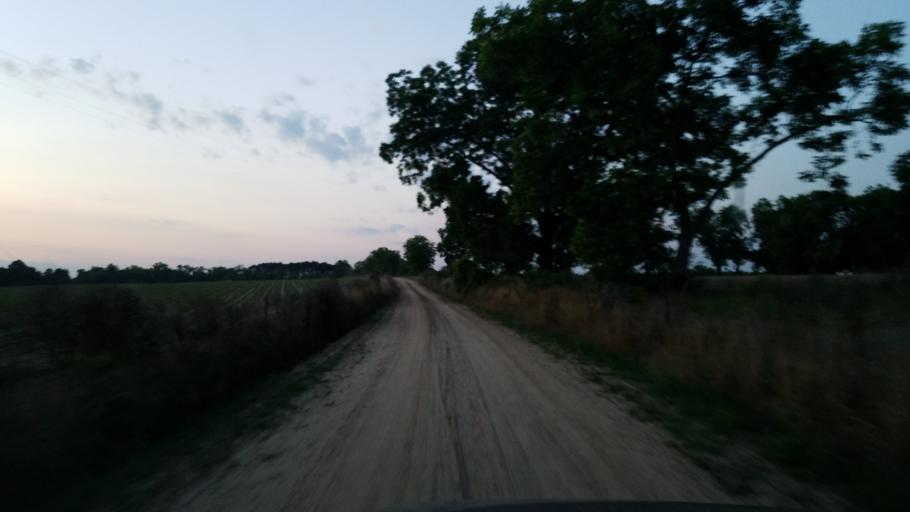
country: US
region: Georgia
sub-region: Turner County
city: Ashburn
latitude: 31.6609
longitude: -83.6262
